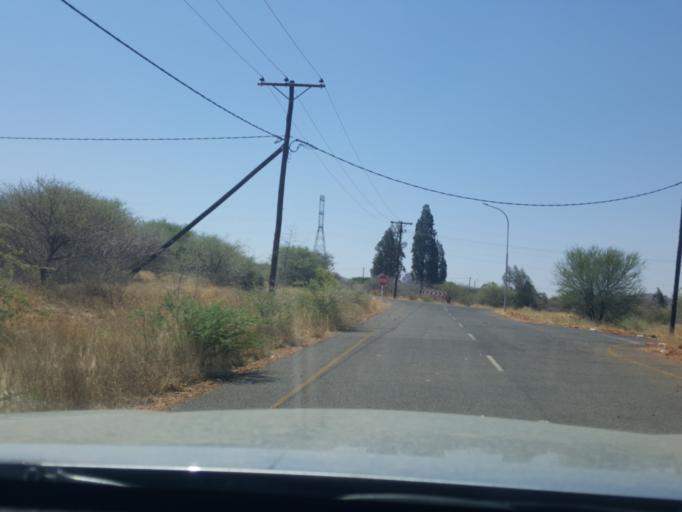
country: BW
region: South East
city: Lobatse
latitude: -25.1804
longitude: 25.6817
